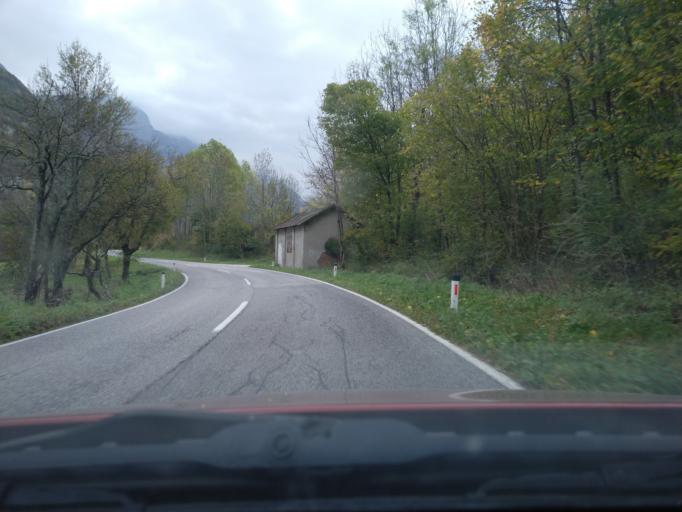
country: SI
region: Bovec
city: Bovec
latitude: 46.2887
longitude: 13.5014
